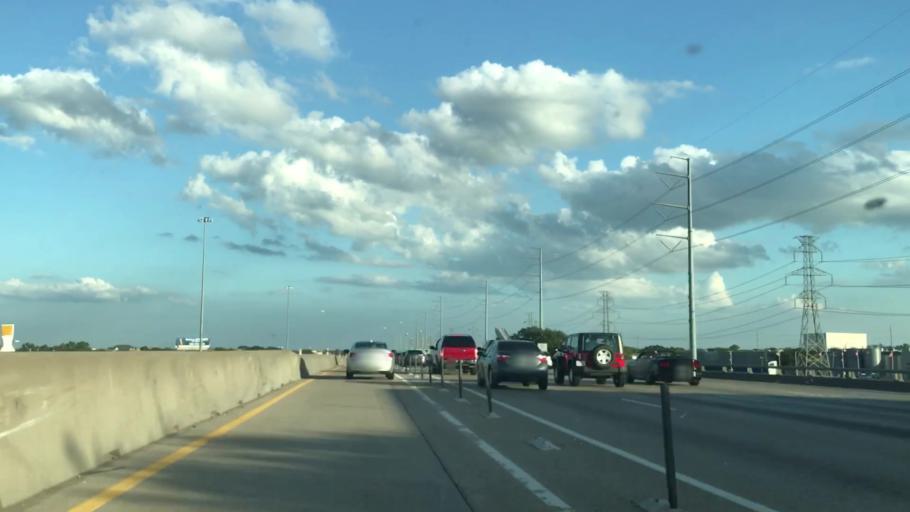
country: US
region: Texas
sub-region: Dallas County
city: Garland
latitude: 32.8644
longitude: -96.6620
